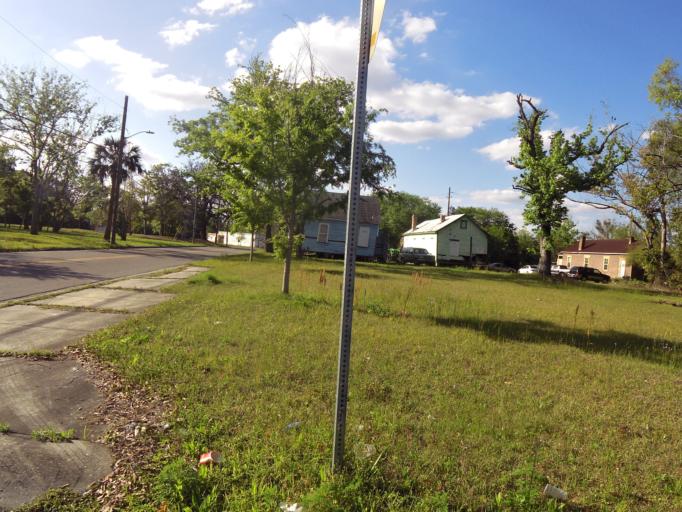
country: US
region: Florida
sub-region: Duval County
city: Jacksonville
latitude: 30.3243
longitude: -81.6771
